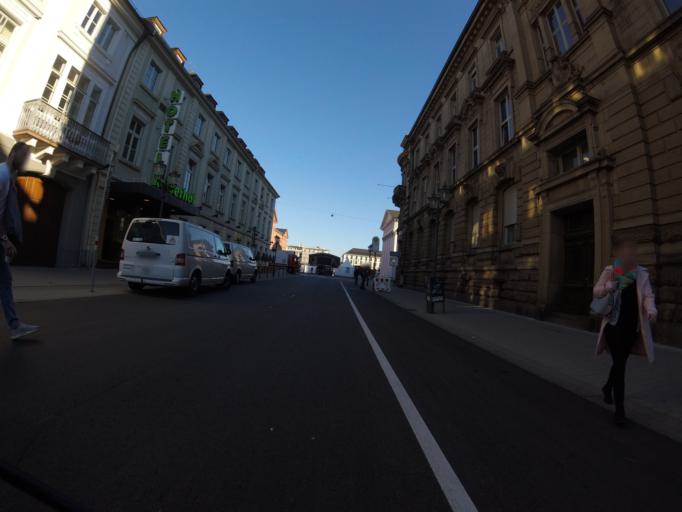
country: DE
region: Baden-Wuerttemberg
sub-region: Karlsruhe Region
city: Karlsruhe
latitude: 49.0077
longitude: 8.4038
